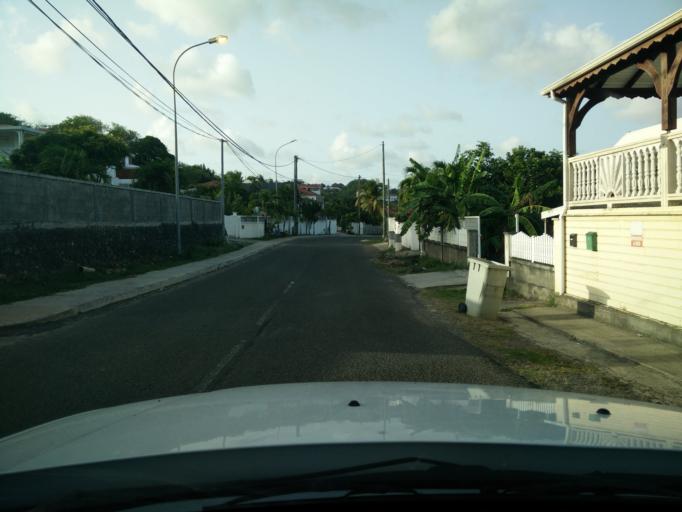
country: GP
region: Guadeloupe
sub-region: Guadeloupe
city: Le Gosier
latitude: 16.2044
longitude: -61.4715
